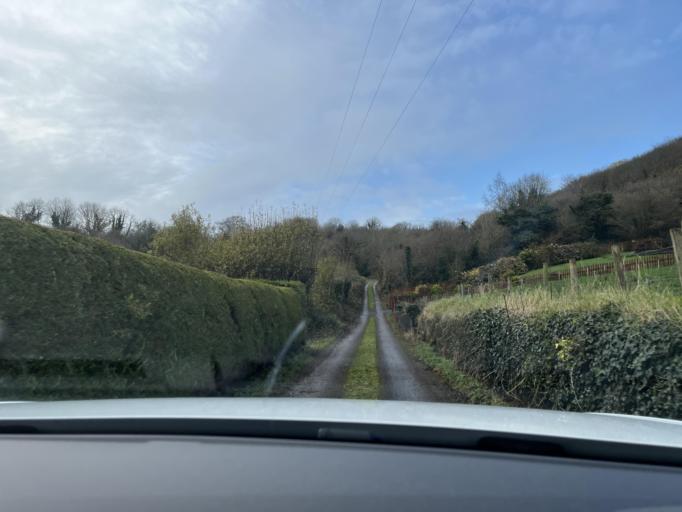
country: IE
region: Connaught
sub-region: Sligo
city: Sligo
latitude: 54.2677
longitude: -8.3489
